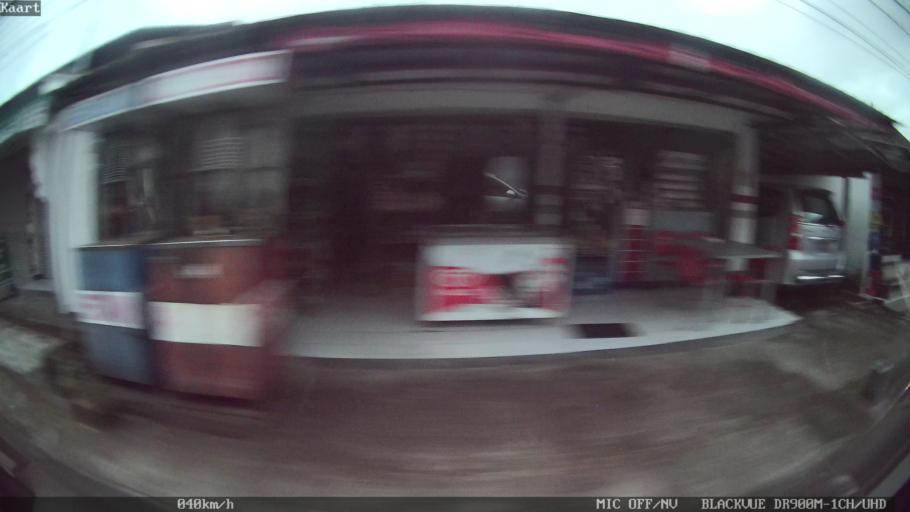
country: ID
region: Bali
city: Banjar Tengah
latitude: -8.4609
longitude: 115.2772
